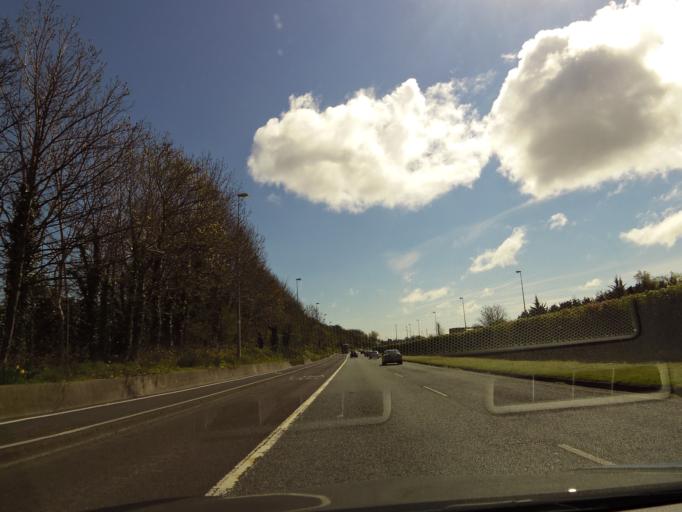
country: IE
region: Leinster
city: Cabinteely
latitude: 53.2696
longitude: -6.1637
